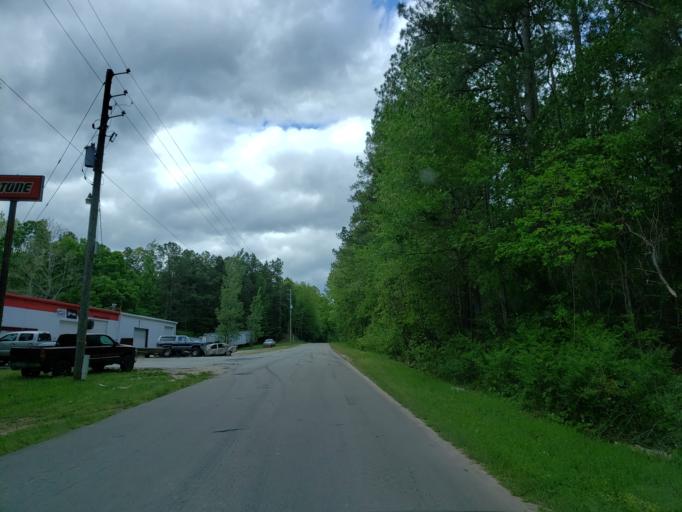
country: US
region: Georgia
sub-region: Haralson County
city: Tallapoosa
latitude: 33.7296
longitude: -85.2921
